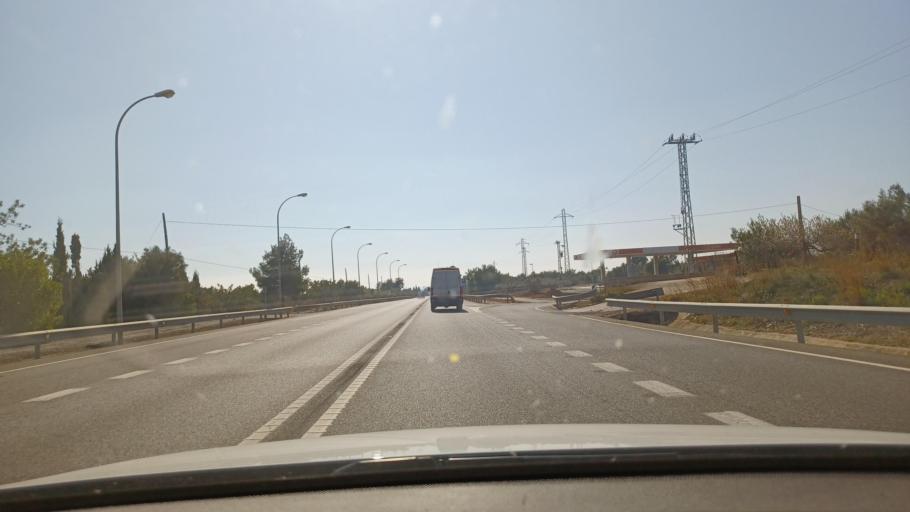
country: ES
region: Catalonia
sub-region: Provincia de Tarragona
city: L'Ampolla
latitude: 40.8362
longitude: 0.7106
